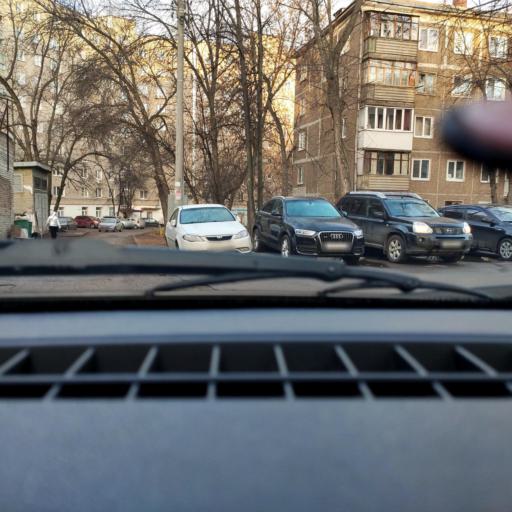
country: RU
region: Bashkortostan
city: Ufa
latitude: 54.7481
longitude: 56.0249
